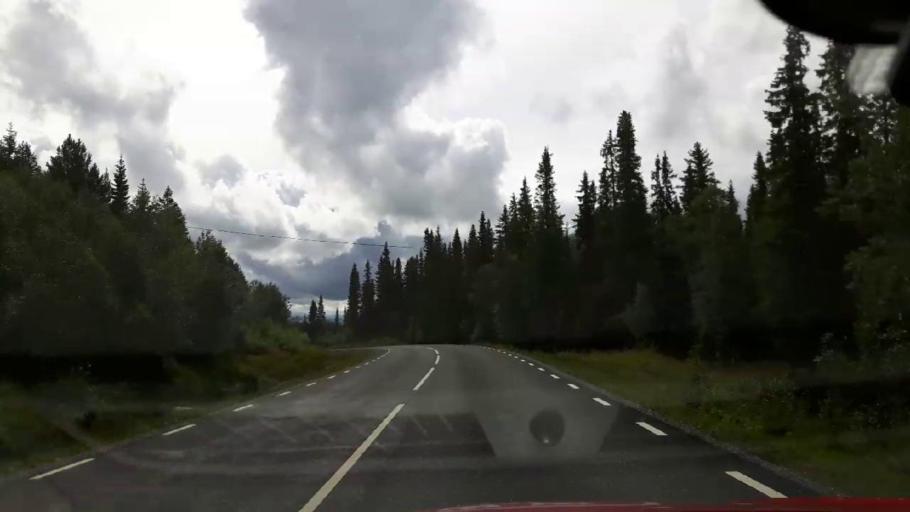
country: NO
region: Nord-Trondelag
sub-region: Lierne
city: Sandvika
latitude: 64.6108
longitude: 14.1188
